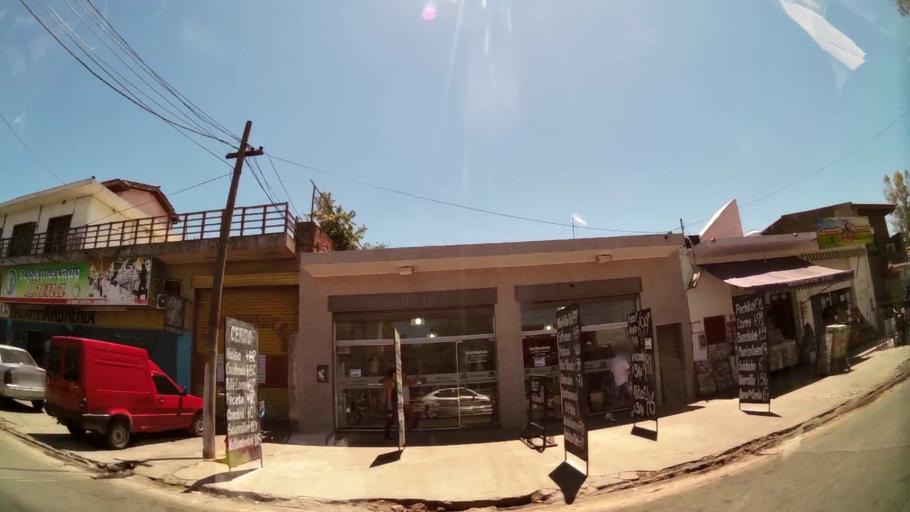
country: AR
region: Buenos Aires
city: Hurlingham
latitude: -34.5087
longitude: -58.7024
